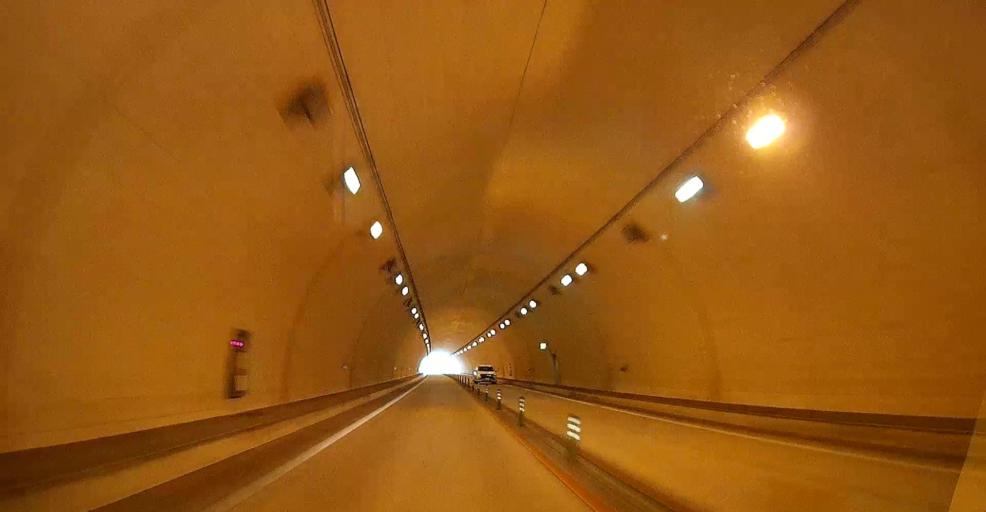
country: JP
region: Kumamoto
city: Hondo
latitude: 32.5081
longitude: 130.3351
